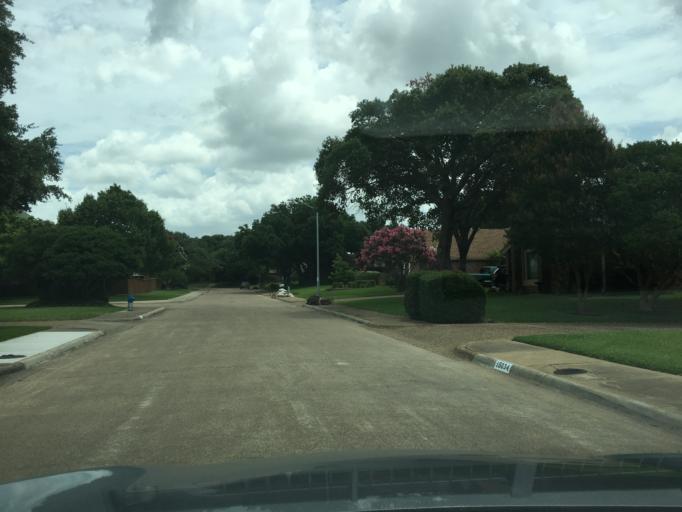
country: US
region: Texas
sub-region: Dallas County
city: Richardson
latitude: 32.9128
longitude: -96.7128
